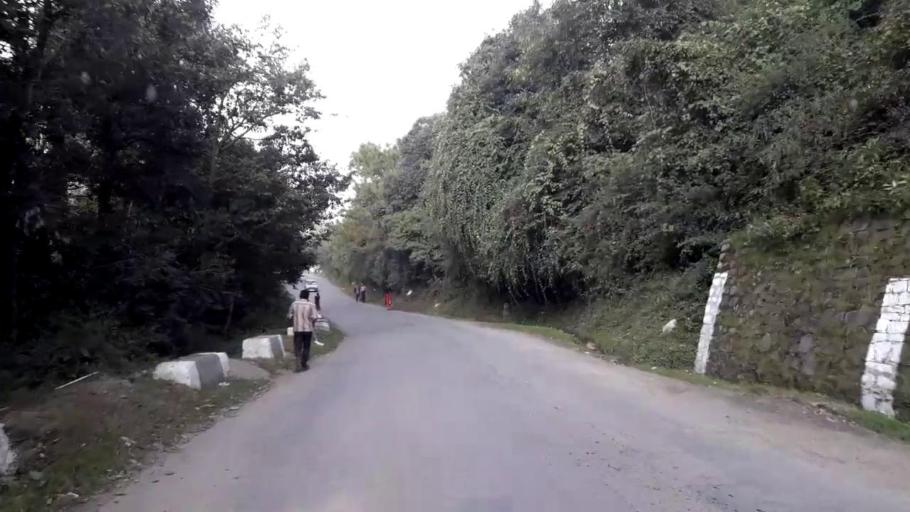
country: IN
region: Himachal Pradesh
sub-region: Shimla
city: Jutogh
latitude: 31.0447
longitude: 77.1304
